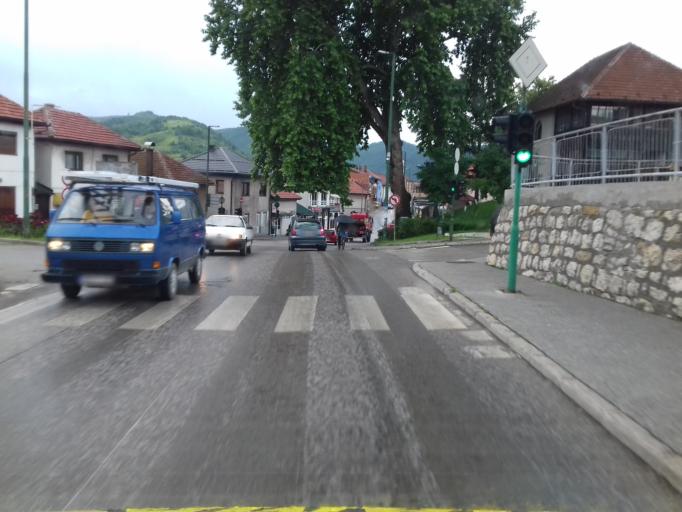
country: BA
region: Federation of Bosnia and Herzegovina
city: Visoko
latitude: 43.9878
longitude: 18.1774
